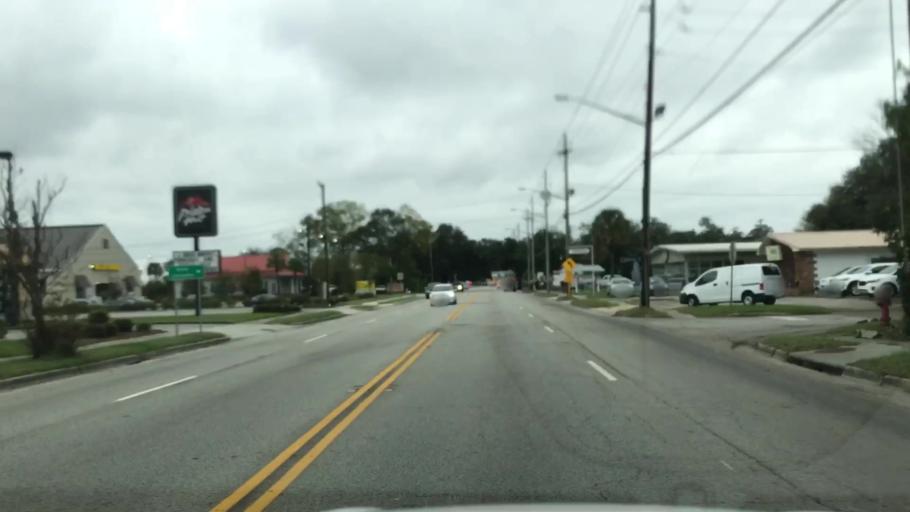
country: US
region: South Carolina
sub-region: Georgetown County
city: Georgetown
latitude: 33.3693
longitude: -79.2769
